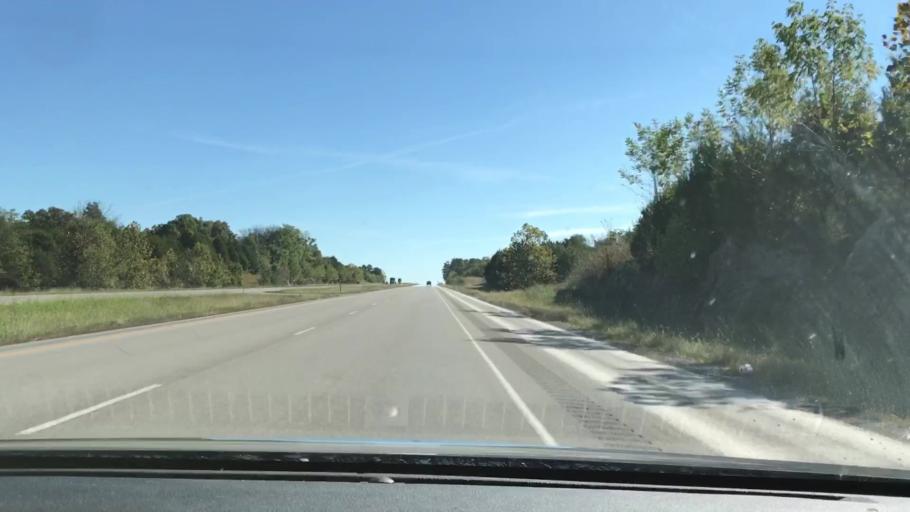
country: US
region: Kentucky
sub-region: Todd County
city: Elkton
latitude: 36.8475
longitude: -87.3209
